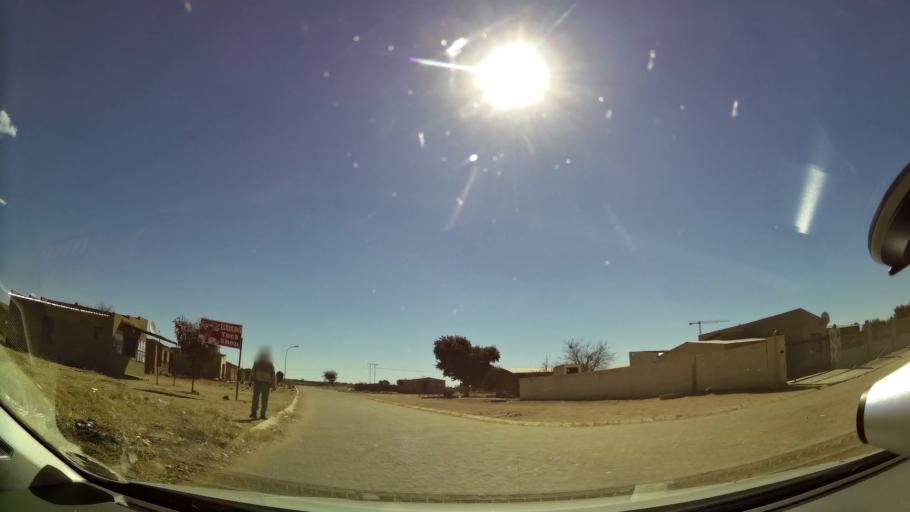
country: ZA
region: North-West
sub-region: Dr Kenneth Kaunda District Municipality
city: Klerksdorp
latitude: -26.8675
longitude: 26.5759
